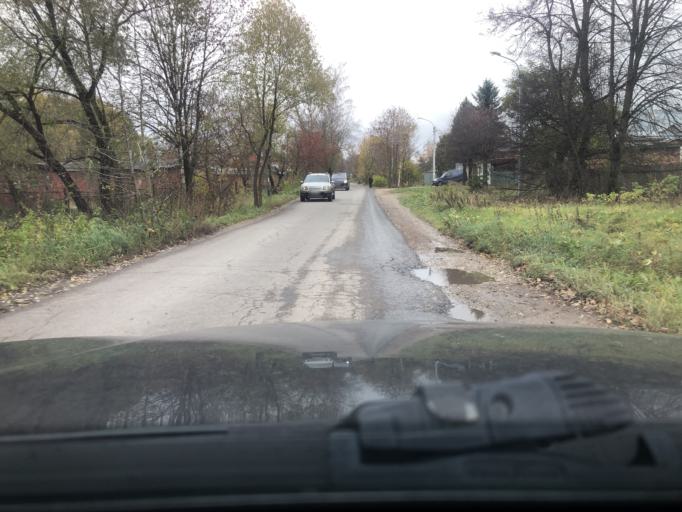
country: RU
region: Moskovskaya
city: Sergiyev Posad
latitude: 56.2968
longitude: 38.1122
